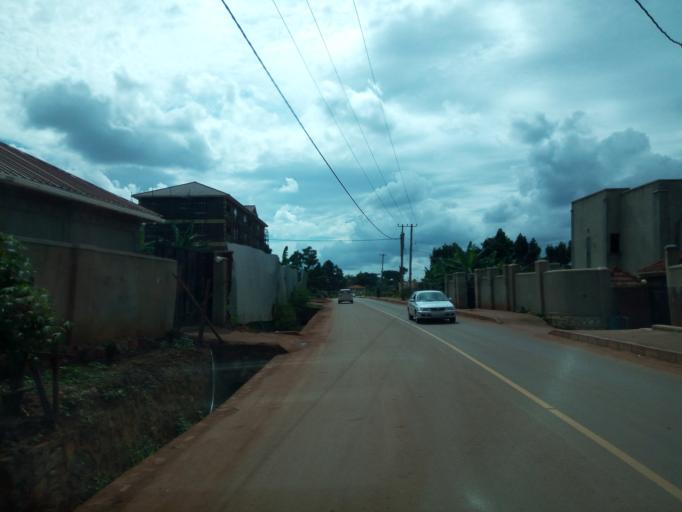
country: UG
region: Central Region
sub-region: Wakiso District
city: Kireka
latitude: 0.3913
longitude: 32.6030
